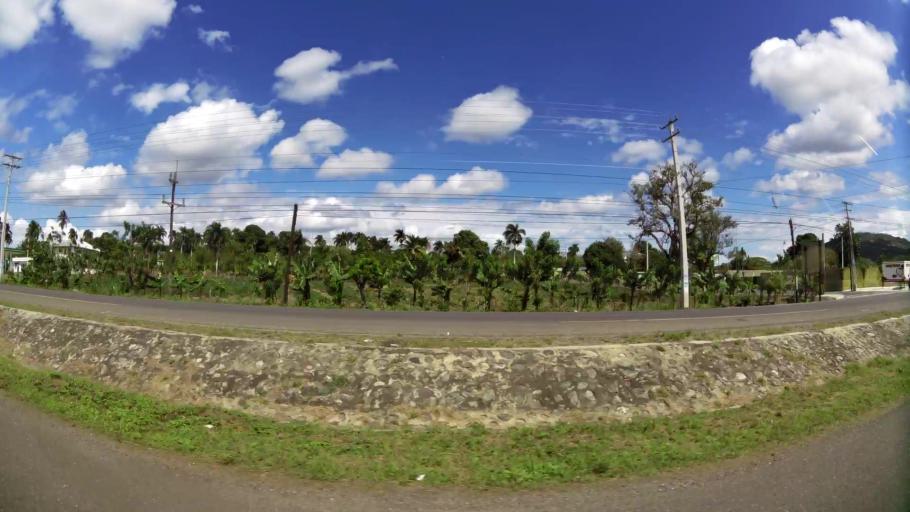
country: DO
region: La Vega
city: Rio Verde Arriba
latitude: 19.3192
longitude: -70.5871
